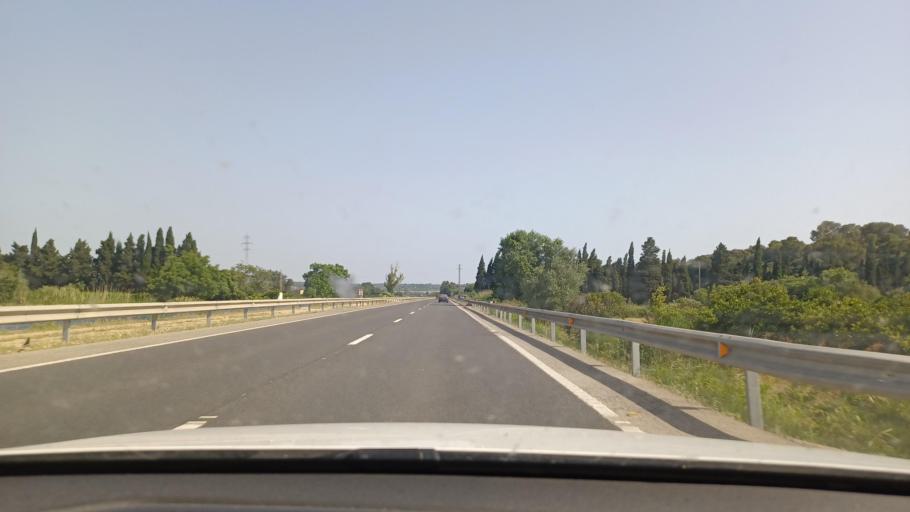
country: ES
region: Catalonia
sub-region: Provincia de Tarragona
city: Tortosa
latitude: 40.7678
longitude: 0.5311
